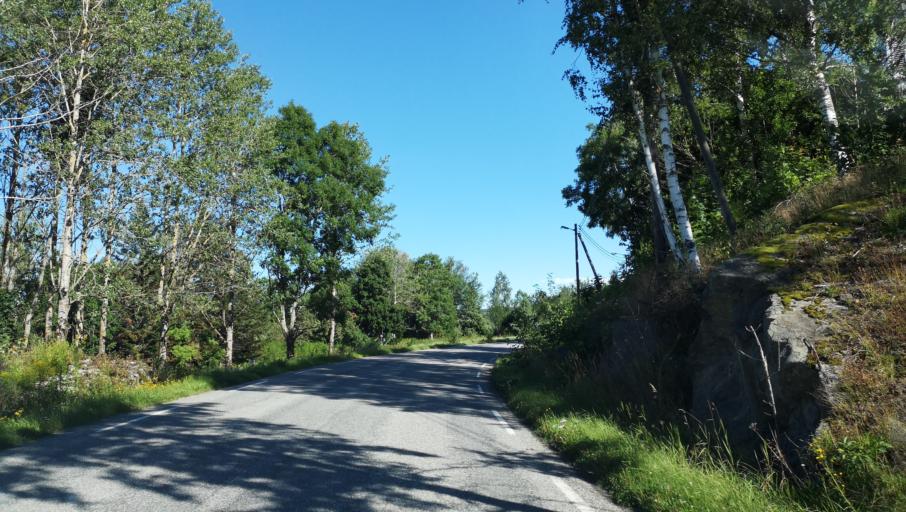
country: NO
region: Ostfold
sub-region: Hobol
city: Tomter
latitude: 59.6508
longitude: 11.0106
